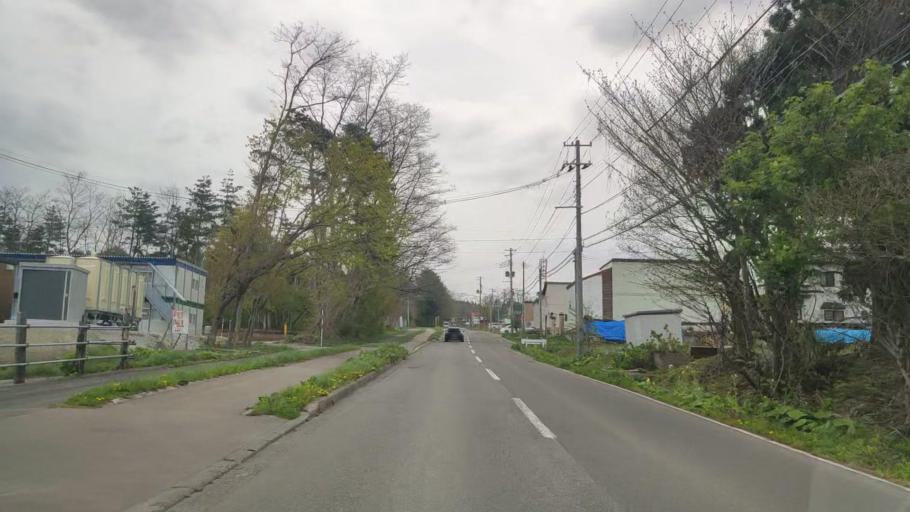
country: JP
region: Aomori
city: Aomori Shi
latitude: 40.7702
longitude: 140.7990
